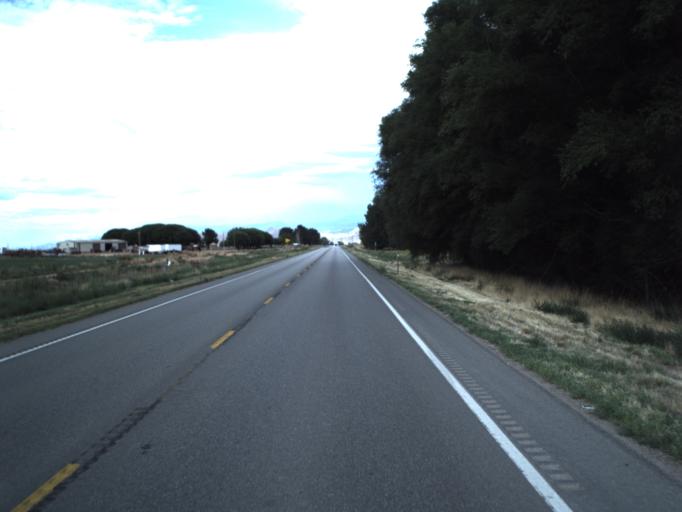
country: US
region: Utah
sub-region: Sevier County
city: Richfield
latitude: 38.7866
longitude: -112.0522
